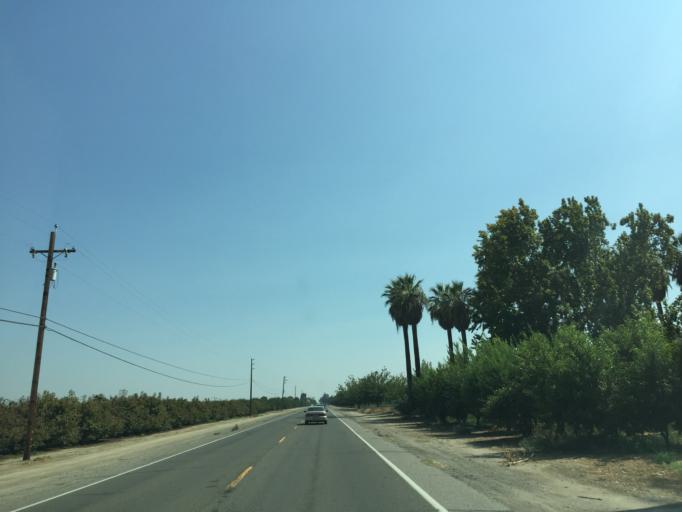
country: US
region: California
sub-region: Kings County
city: Lucerne
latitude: 36.3810
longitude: -119.6731
